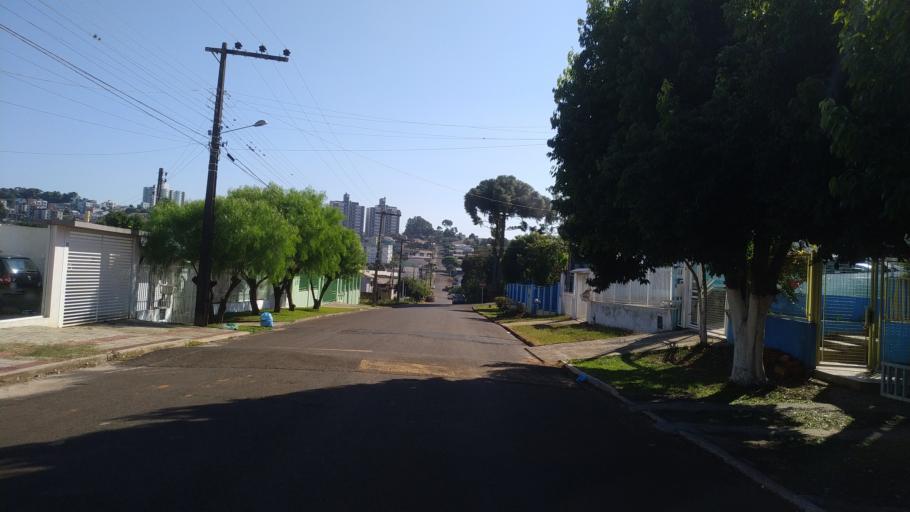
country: BR
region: Santa Catarina
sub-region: Chapeco
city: Chapeco
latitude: -27.0792
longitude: -52.6067
